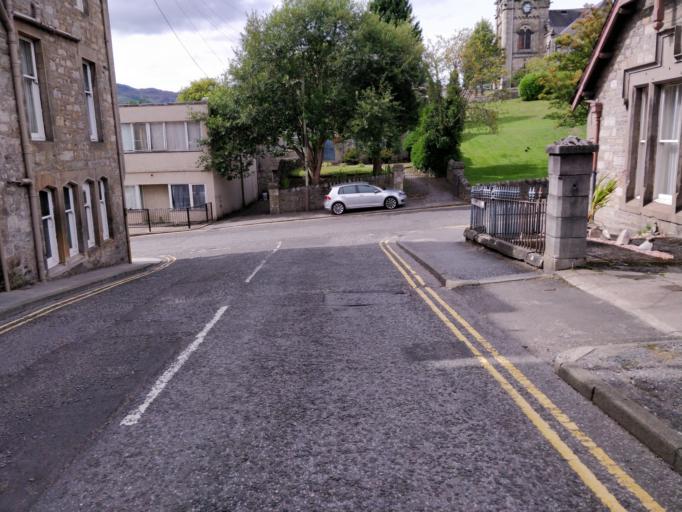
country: GB
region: Scotland
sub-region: Perth and Kinross
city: Pitlochry
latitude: 56.7037
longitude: -3.7315
